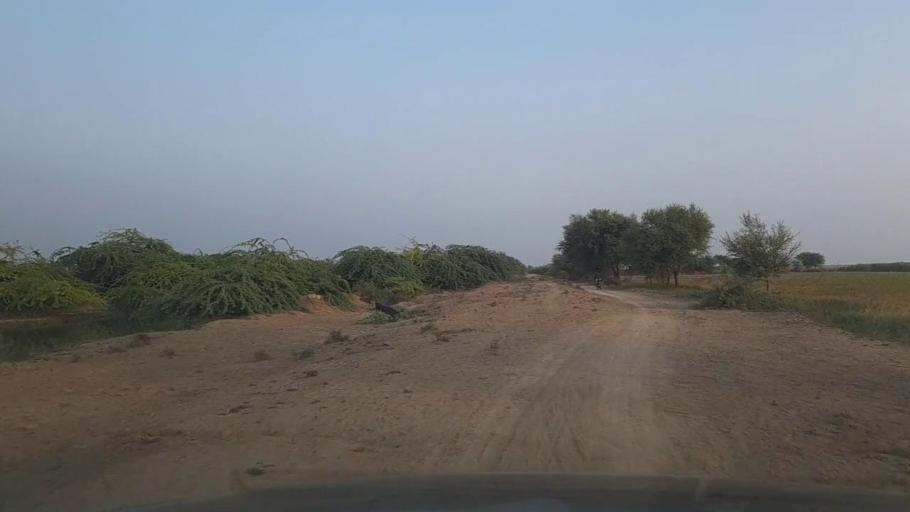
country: PK
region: Sindh
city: Jati
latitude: 24.5384
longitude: 68.4043
